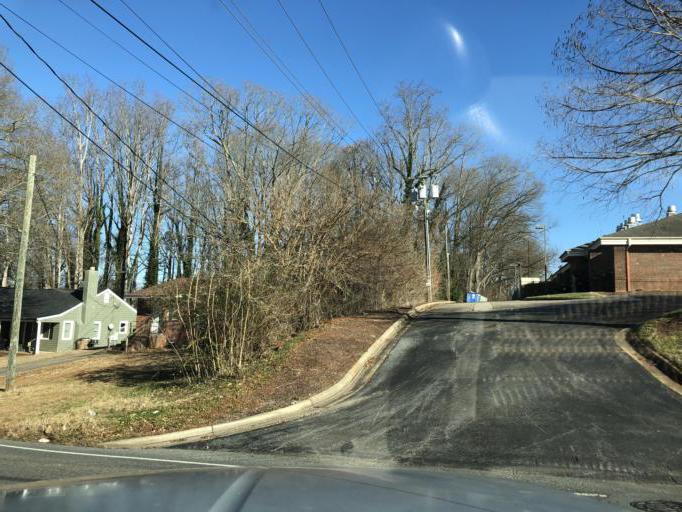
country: US
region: North Carolina
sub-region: Cleveland County
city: Shelby
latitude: 35.3051
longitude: -81.5395
